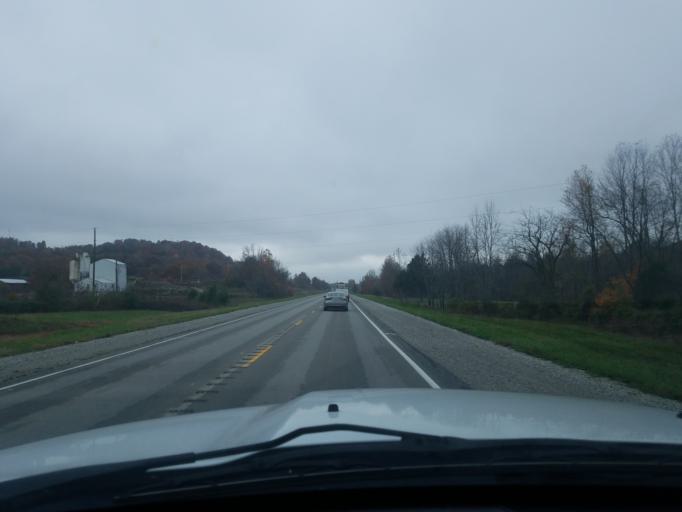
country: US
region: Kentucky
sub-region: Marion County
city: Lebanon
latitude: 37.5218
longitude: -85.3001
